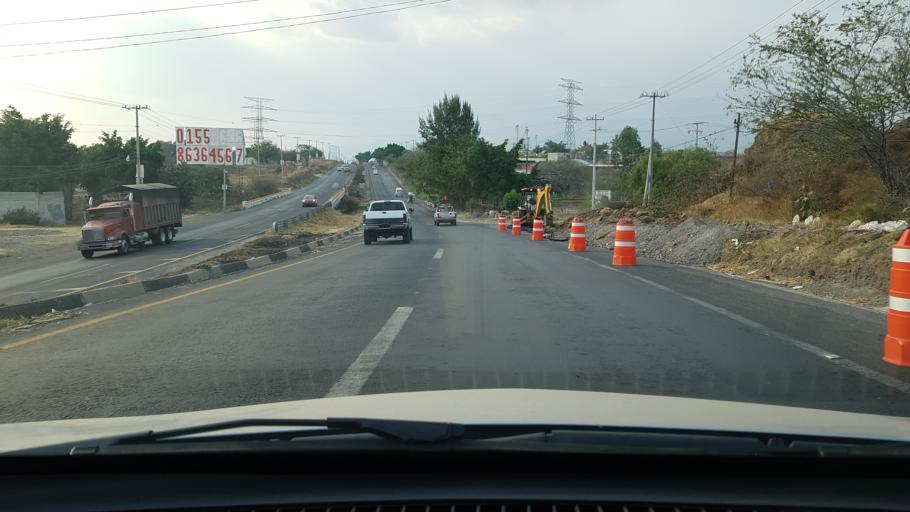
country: MX
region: Morelos
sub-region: Yecapixtla
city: Juan Morales
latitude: 18.8396
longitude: -98.9246
